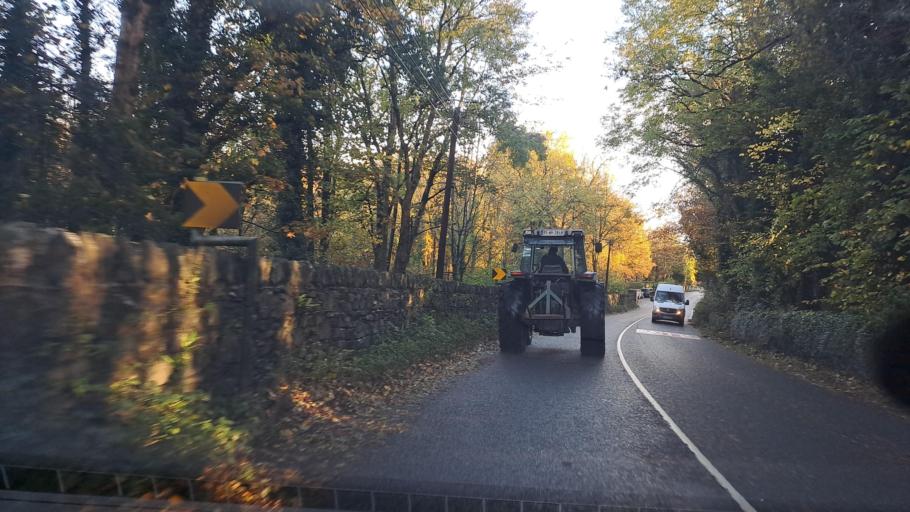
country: IE
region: Ulster
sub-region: County Monaghan
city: Monaghan
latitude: 54.2172
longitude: -6.9839
